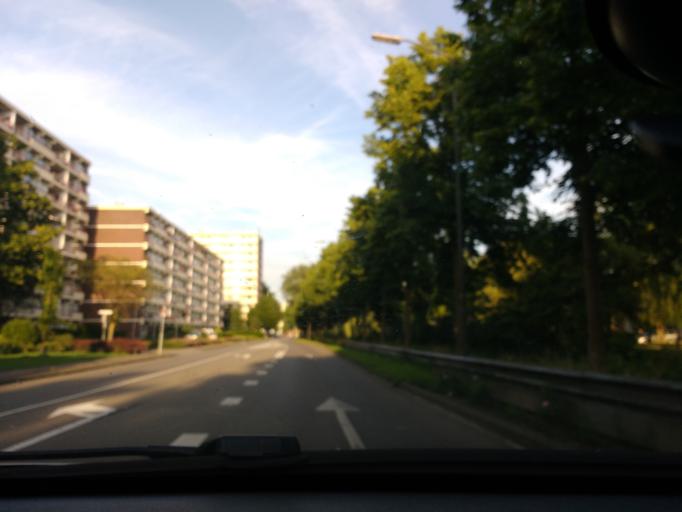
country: NL
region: Utrecht
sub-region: Gemeente Veenendaal
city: Veenendaal
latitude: 52.0245
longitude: 5.5488
